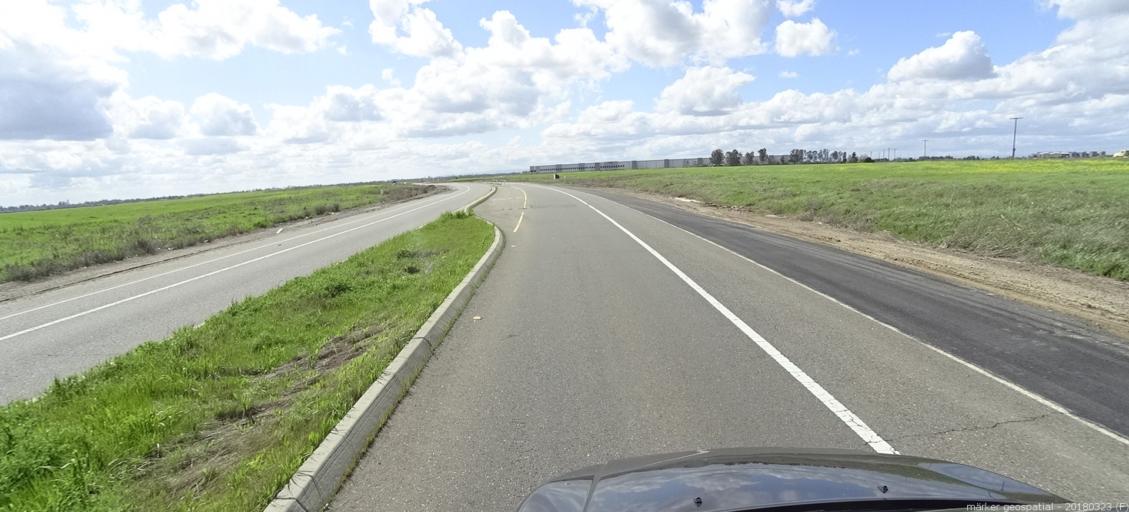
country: US
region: California
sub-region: Sacramento County
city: Elverta
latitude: 38.6850
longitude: -121.5632
